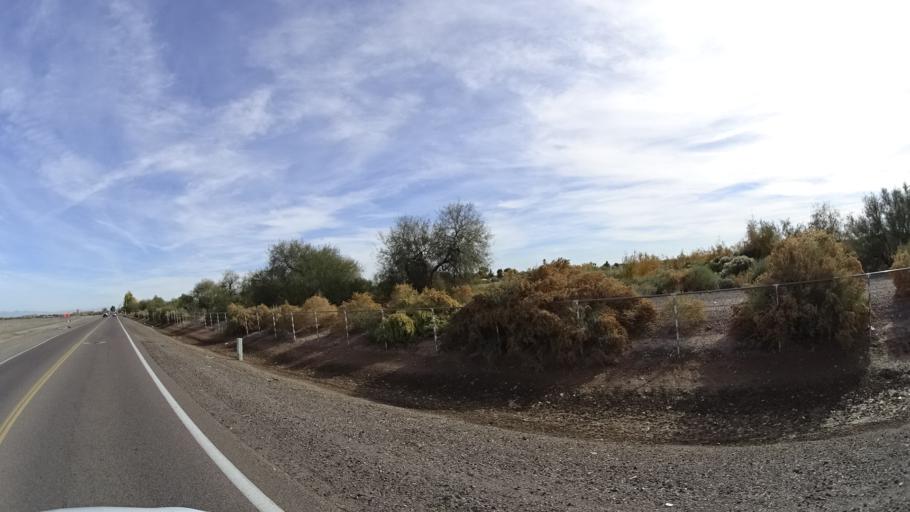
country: US
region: Arizona
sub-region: Maricopa County
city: Chandler
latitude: 33.2624
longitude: -111.8182
